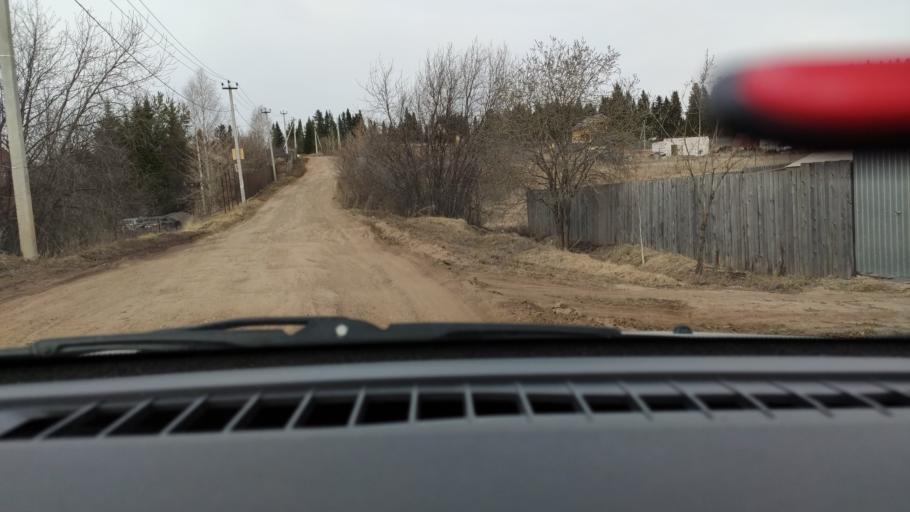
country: RU
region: Perm
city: Kultayevo
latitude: 57.8970
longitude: 56.0143
